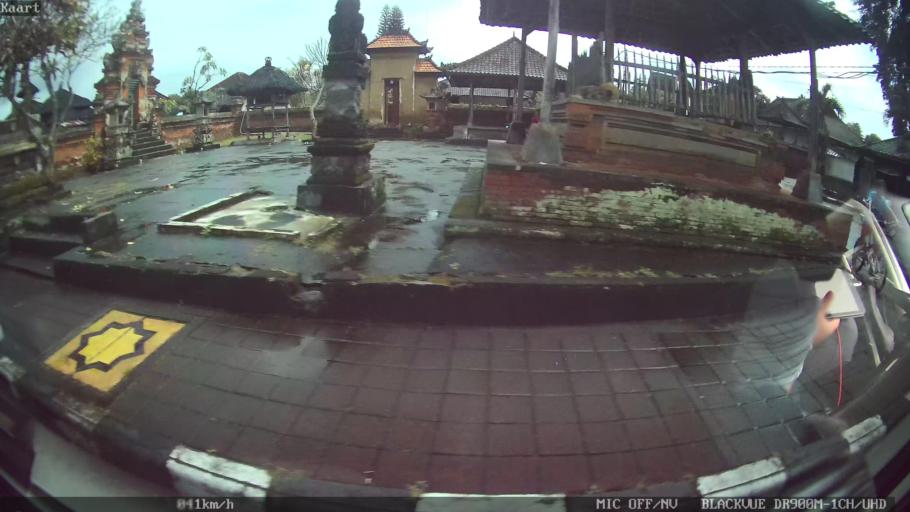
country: ID
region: Bali
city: Pegongan
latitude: -8.4881
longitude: 115.2263
